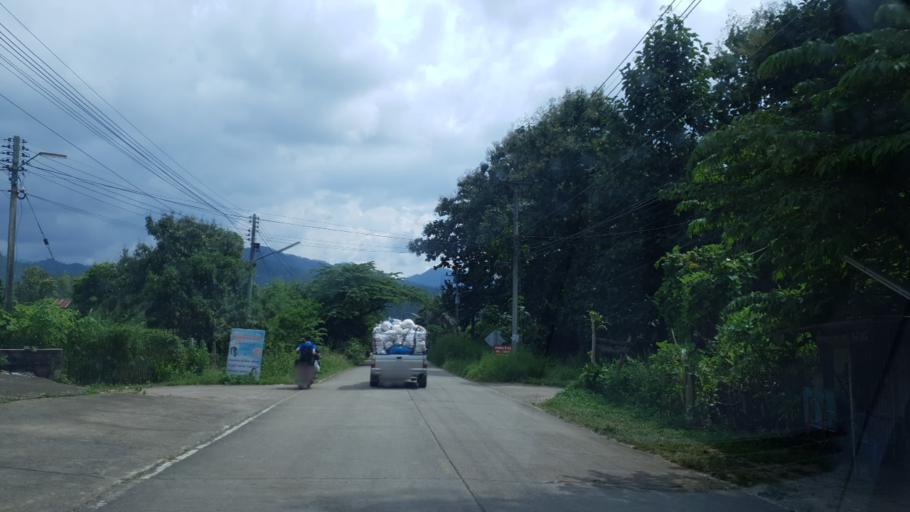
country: TH
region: Mae Hong Son
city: Khun Yuam
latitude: 18.8179
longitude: 97.9322
